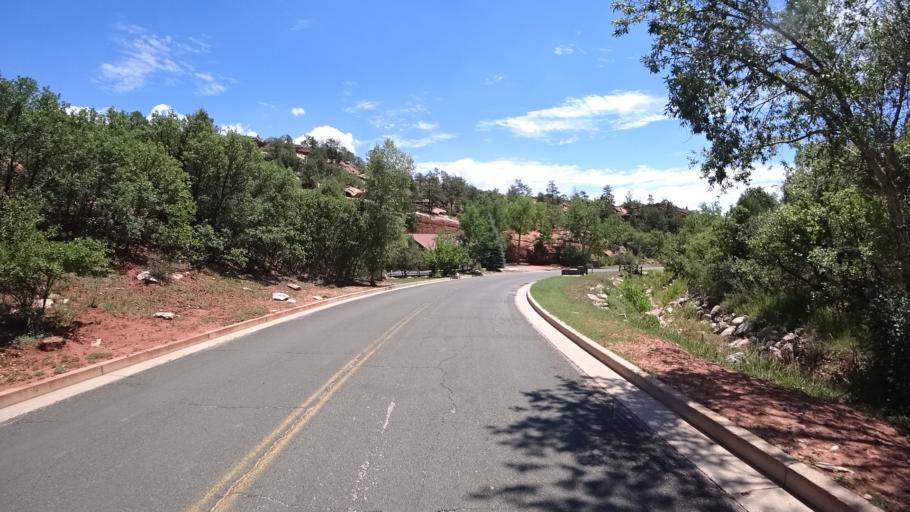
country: US
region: Colorado
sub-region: El Paso County
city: Manitou Springs
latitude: 38.8623
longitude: -104.9001
